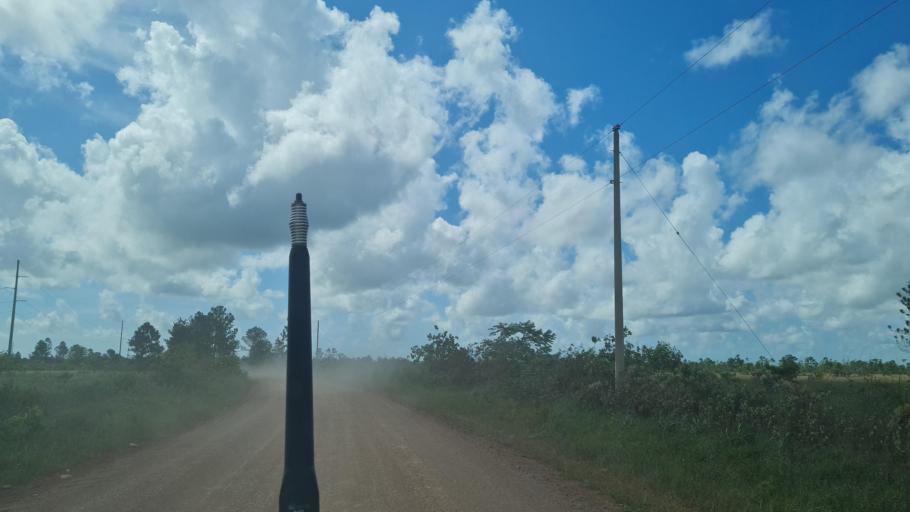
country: NI
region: Atlantico Norte (RAAN)
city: Puerto Cabezas
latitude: 14.1075
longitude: -83.5639
